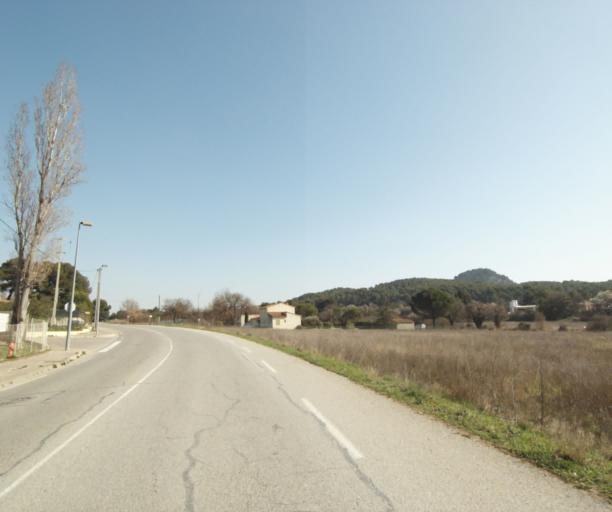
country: FR
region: Provence-Alpes-Cote d'Azur
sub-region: Departement des Bouches-du-Rhone
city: Simiane-Collongue
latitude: 43.4475
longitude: 5.4368
